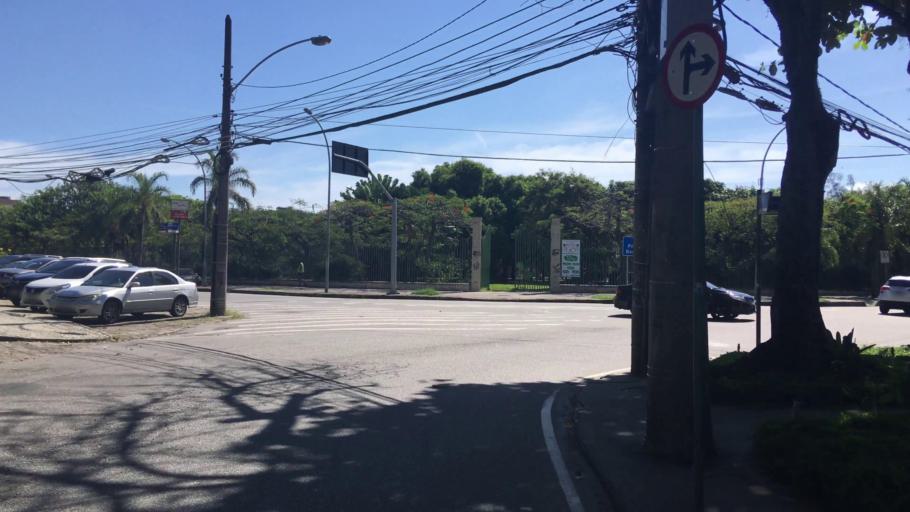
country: BR
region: Rio de Janeiro
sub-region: Rio De Janeiro
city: Rio de Janeiro
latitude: -23.0104
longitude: -43.3085
